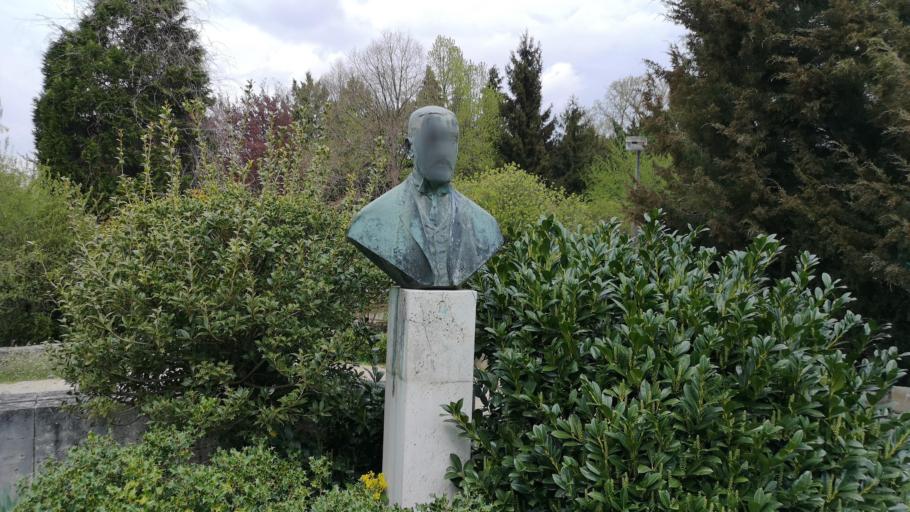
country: SK
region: Nitriansky
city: Zlate Moravce
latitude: 48.3196
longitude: 18.3684
